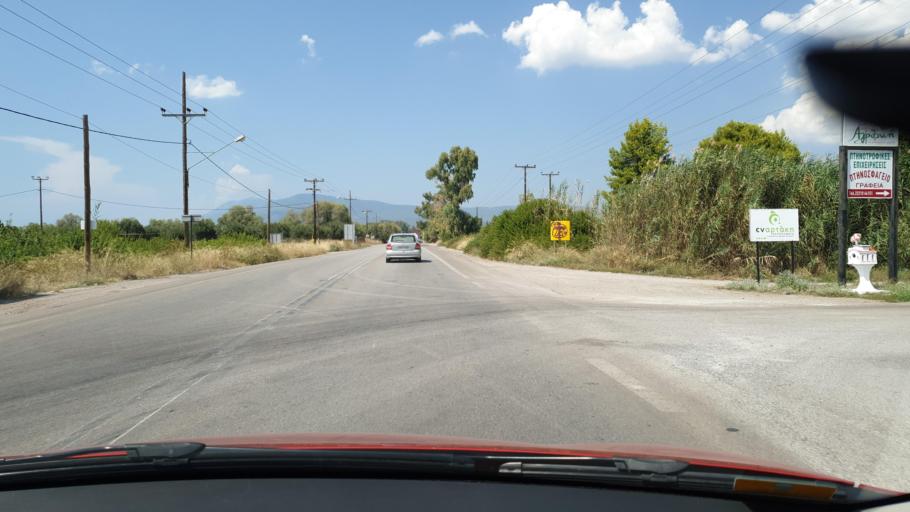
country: GR
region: Central Greece
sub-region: Nomos Evvoias
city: Nea Artaki
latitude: 38.5375
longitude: 23.6308
